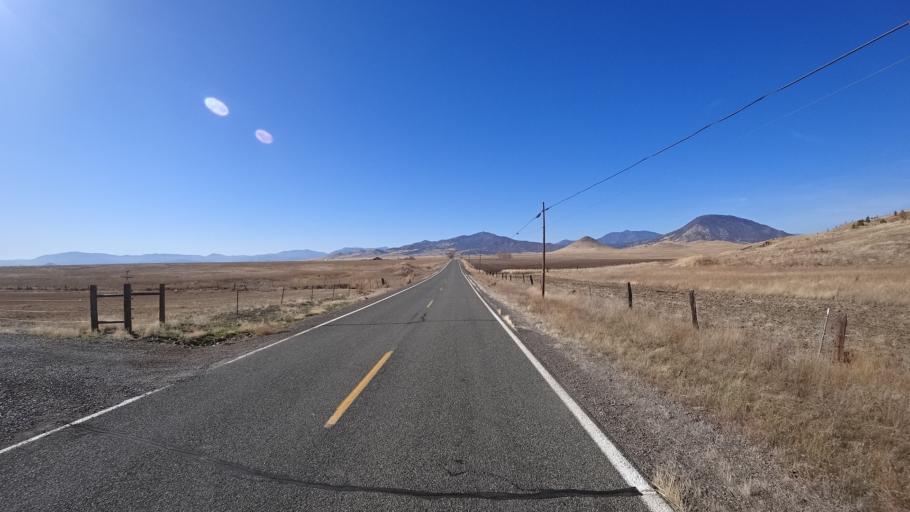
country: US
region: California
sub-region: Siskiyou County
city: Montague
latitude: 41.8082
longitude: -122.4299
